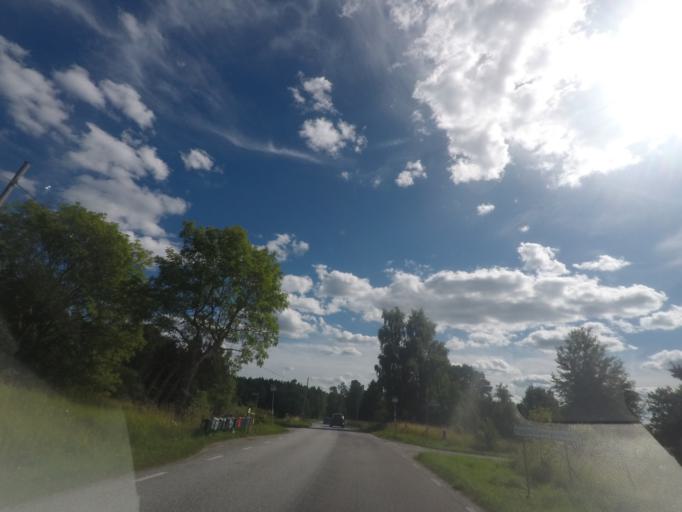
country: SE
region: Stockholm
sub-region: Norrtalje Kommun
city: Arno
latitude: 60.1302
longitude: 18.7790
